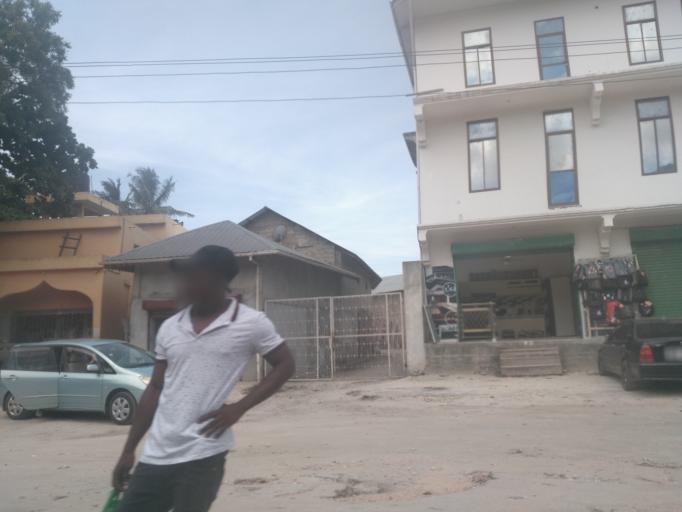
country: TZ
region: Zanzibar Urban/West
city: Zanzibar
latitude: -6.1561
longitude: 39.2054
